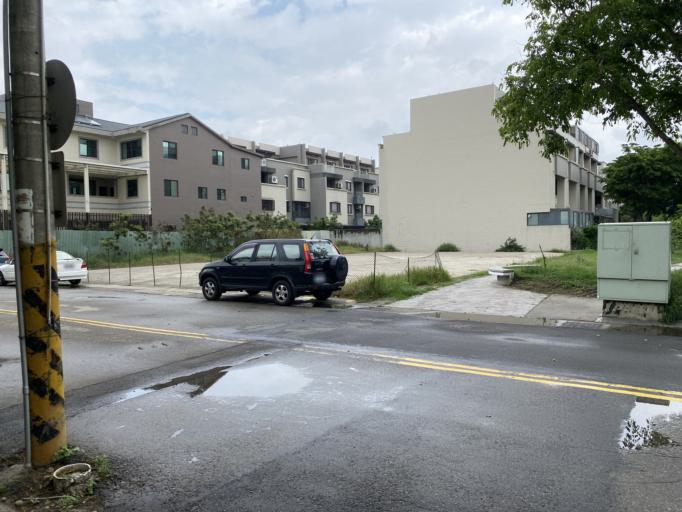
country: TW
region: Taiwan
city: Fengyuan
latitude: 24.2552
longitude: 120.5344
